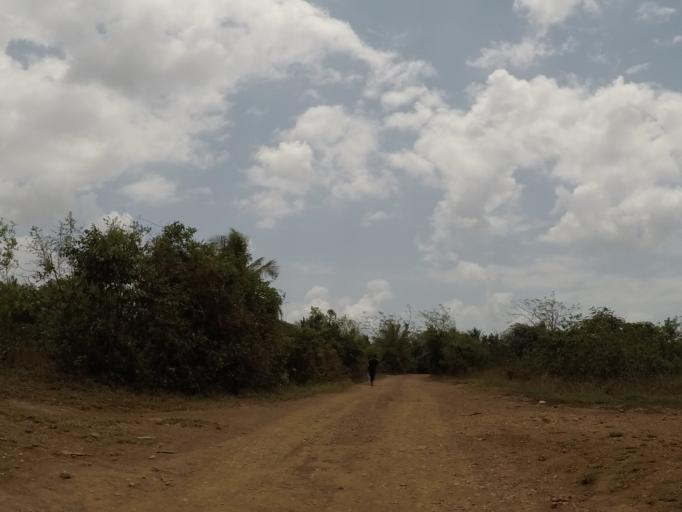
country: TZ
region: Zanzibar Central/South
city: Koani
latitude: -6.1909
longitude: 39.3078
